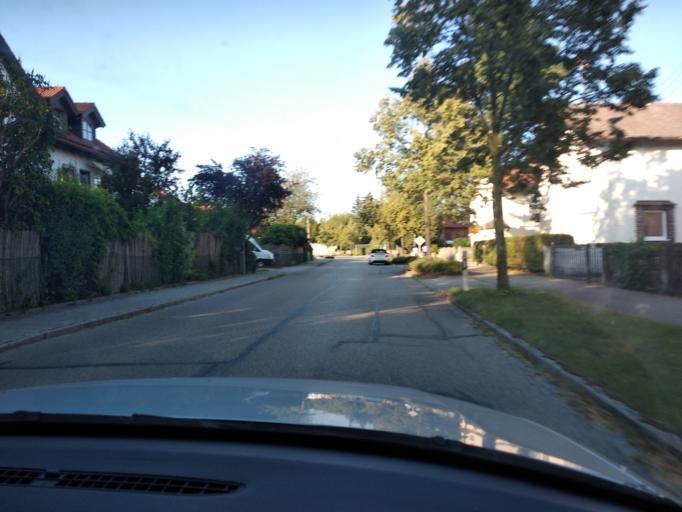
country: DE
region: Bavaria
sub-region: Upper Bavaria
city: Forstinning
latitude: 48.1625
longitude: 11.9054
